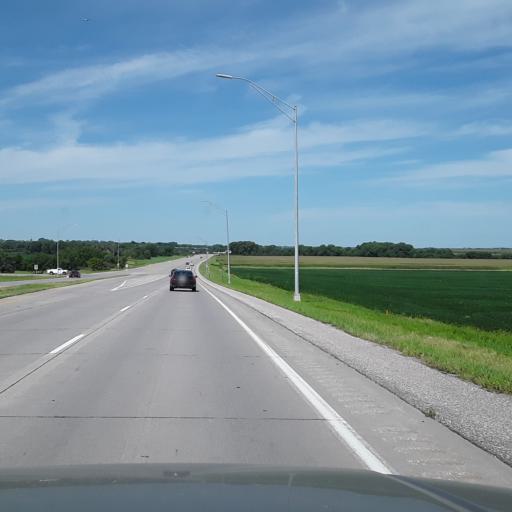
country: US
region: Nebraska
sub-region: Lancaster County
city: Lincoln
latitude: 40.8796
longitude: -96.7620
